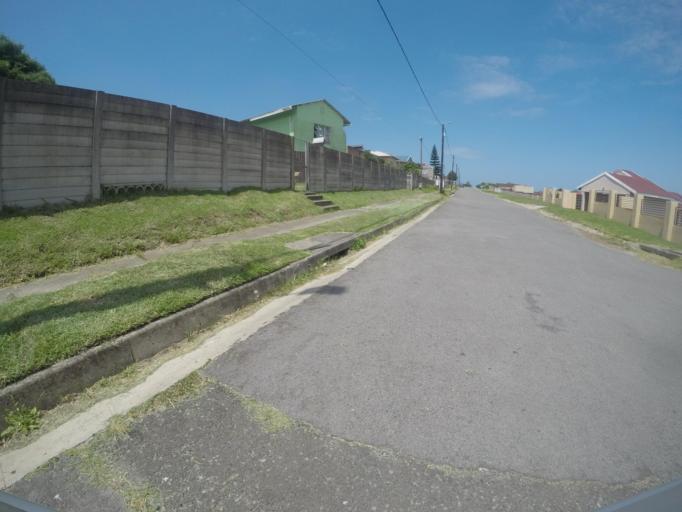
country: ZA
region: Eastern Cape
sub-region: Buffalo City Metropolitan Municipality
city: East London
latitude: -32.9707
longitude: 27.8644
